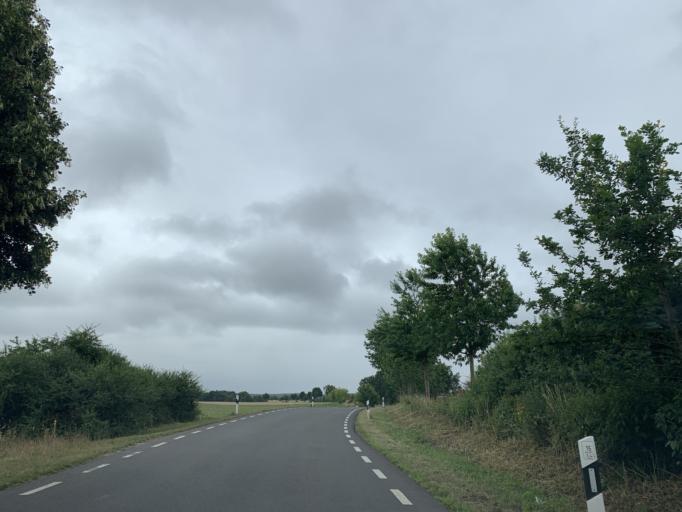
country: DE
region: Mecklenburg-Vorpommern
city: Loitz
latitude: 53.3115
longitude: 13.4192
